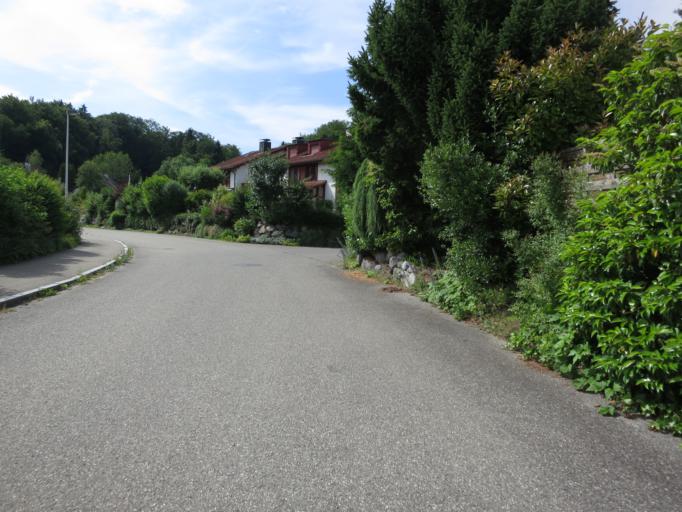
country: CH
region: Zurich
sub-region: Bezirk Meilen
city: Hombrechtikon
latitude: 47.2558
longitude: 8.7792
